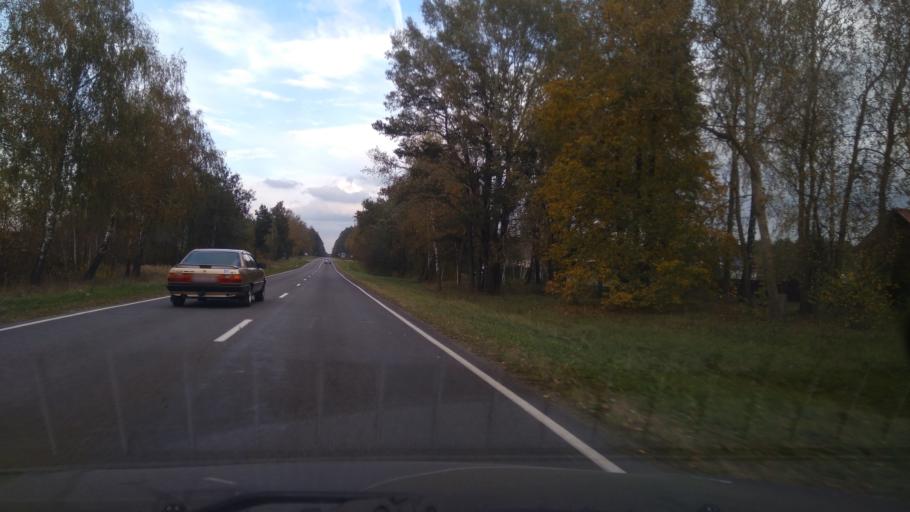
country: BY
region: Minsk
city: Rudzyensk
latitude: 53.6222
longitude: 27.8630
